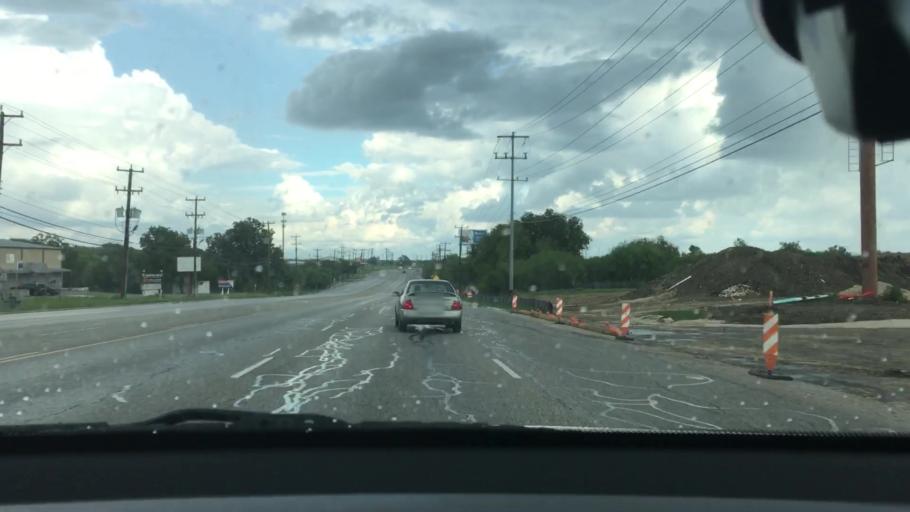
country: US
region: Texas
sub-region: Bexar County
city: Windcrest
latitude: 29.5010
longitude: -98.3573
